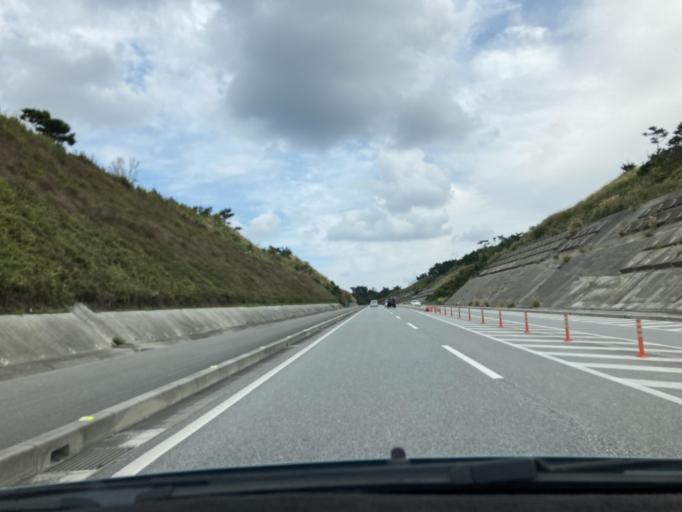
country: JP
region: Okinawa
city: Ishikawa
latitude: 26.4701
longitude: 127.8353
